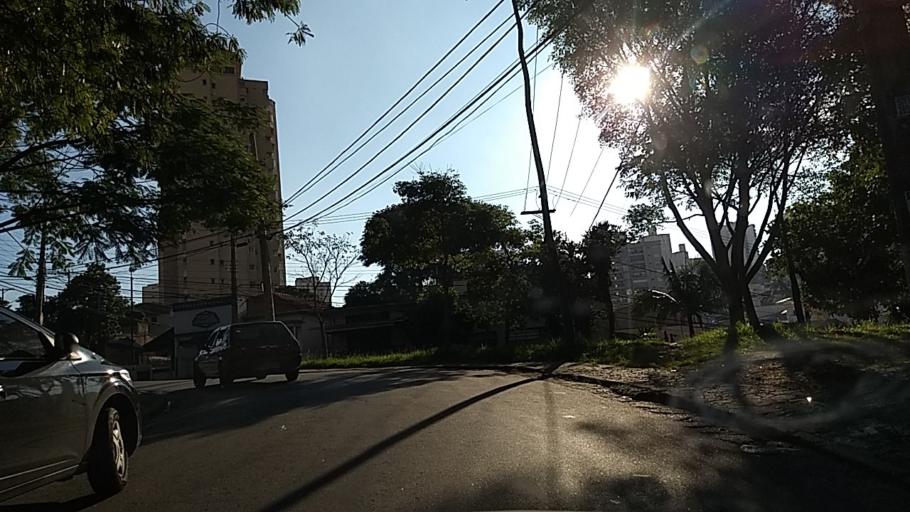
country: BR
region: Sao Paulo
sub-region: Sao Paulo
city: Sao Paulo
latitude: -23.4873
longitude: -46.6110
